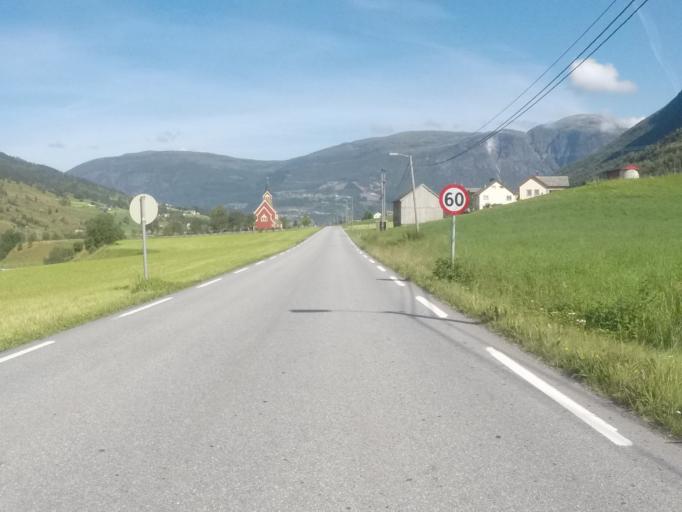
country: NO
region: Sogn og Fjordane
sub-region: Stryn
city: Stryn
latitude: 61.8248
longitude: 6.8093
